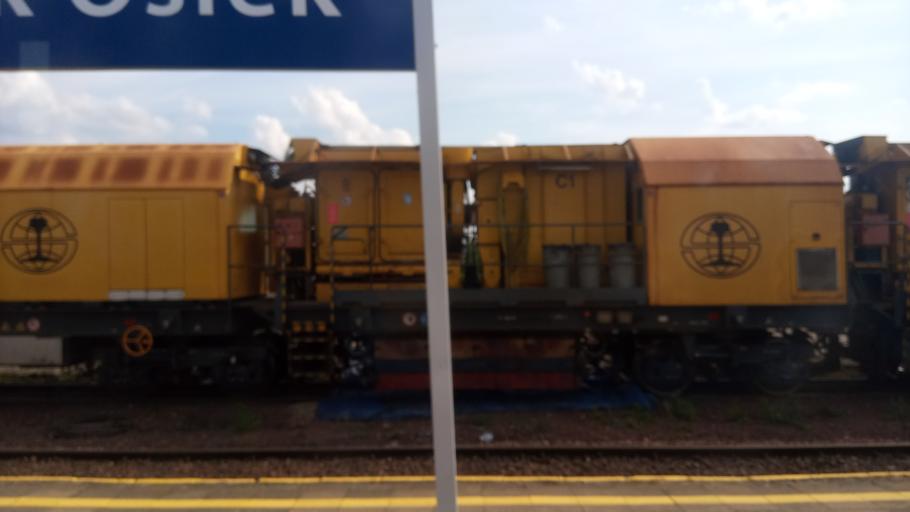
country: PL
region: Greater Poland Voivodeship
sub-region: Powiat pilski
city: Osiek nad Notecia
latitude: 53.1192
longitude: 17.2959
